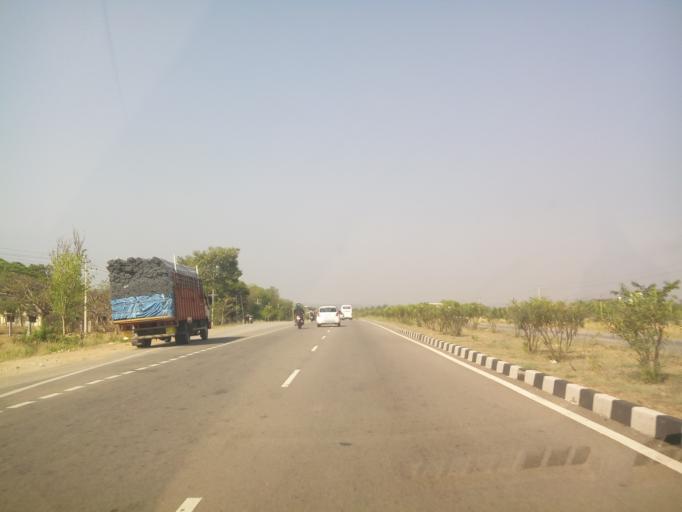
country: IN
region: Karnataka
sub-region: Mandya
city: Belluru
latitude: 12.9892
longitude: 76.8796
